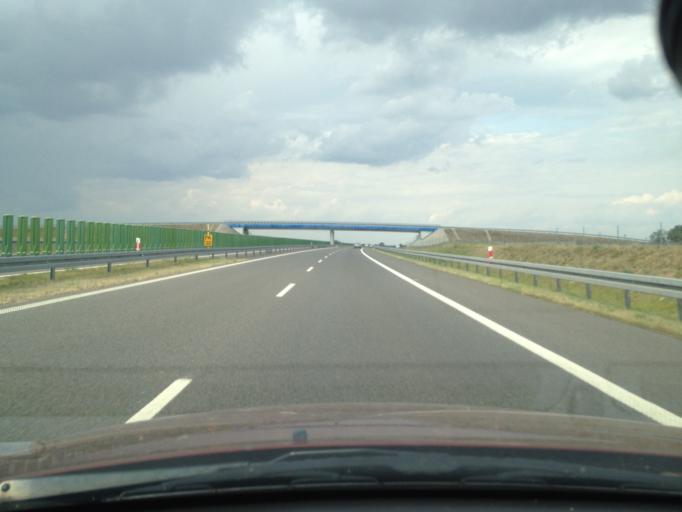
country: PL
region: West Pomeranian Voivodeship
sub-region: Powiat pyrzycki
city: Kozielice
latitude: 53.1043
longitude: 14.7692
